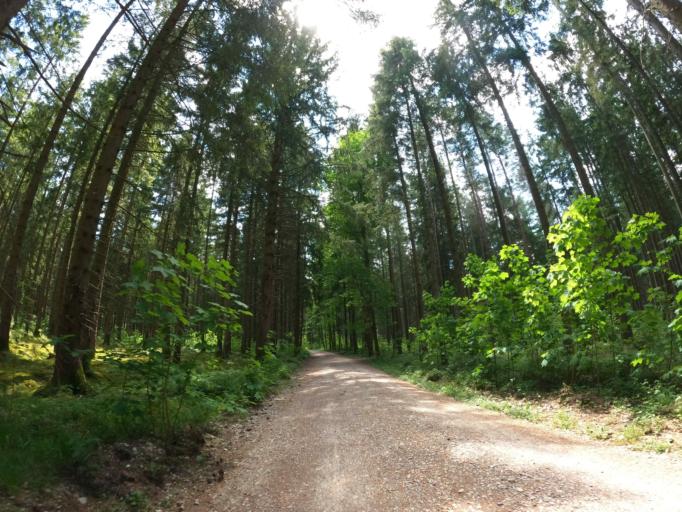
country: DE
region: Bavaria
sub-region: Upper Bavaria
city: Oberhaching
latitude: 48.0165
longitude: 11.6260
